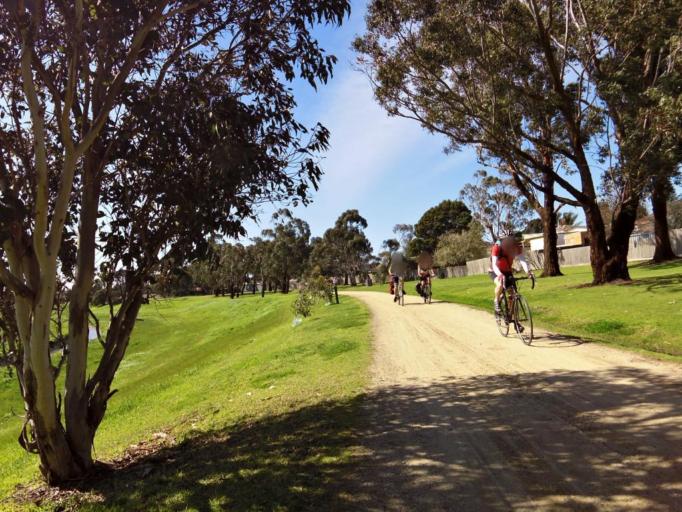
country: AU
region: Victoria
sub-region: Greater Dandenong
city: Dandenong
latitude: -37.9961
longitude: 145.2001
